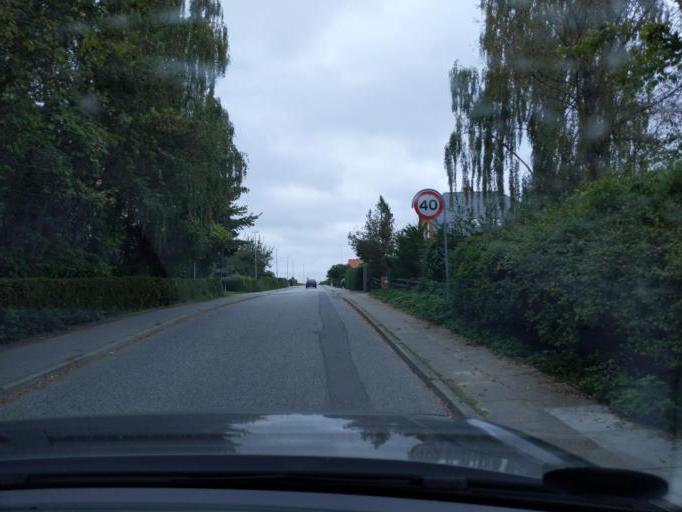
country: DK
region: Central Jutland
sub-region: Randers Kommune
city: Randers
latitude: 56.4759
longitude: 9.9907
